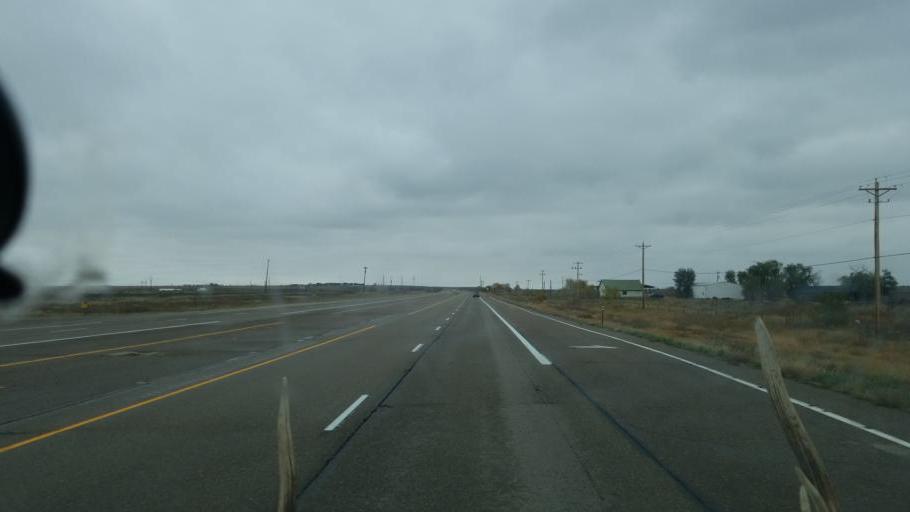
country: US
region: Colorado
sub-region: Pueblo County
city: Pueblo
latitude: 38.2695
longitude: -104.4029
